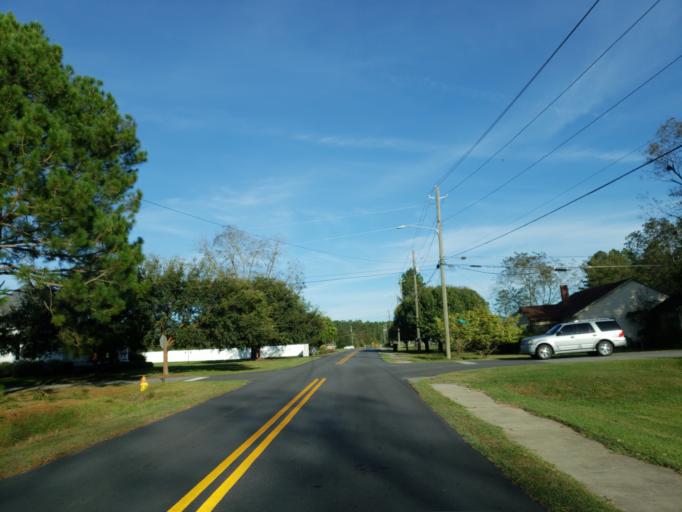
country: US
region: Georgia
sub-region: Dooly County
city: Vienna
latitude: 32.0982
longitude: -83.7907
